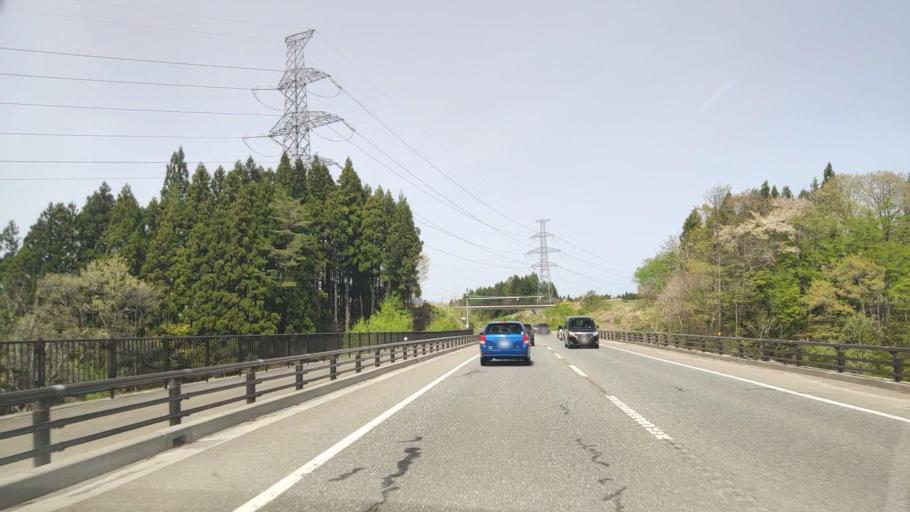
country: JP
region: Aomori
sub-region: Misawa Shi
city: Inuotose
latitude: 40.6827
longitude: 141.1705
